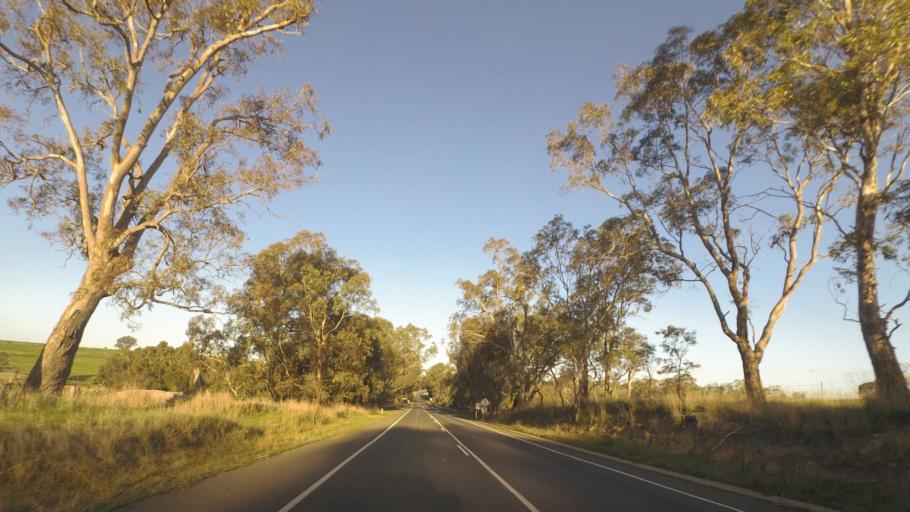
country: AU
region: Victoria
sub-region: Mount Alexander
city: Castlemaine
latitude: -37.0929
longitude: 144.5071
